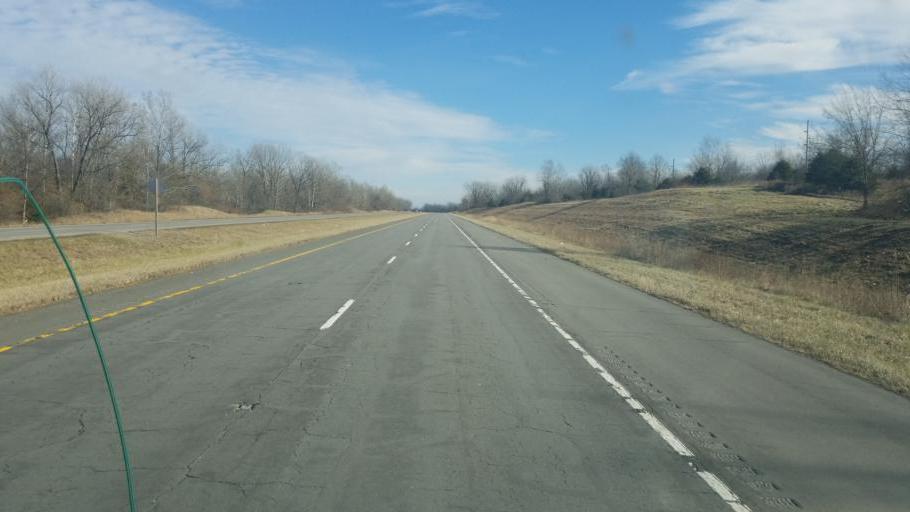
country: US
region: Illinois
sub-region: Saline County
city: Carrier Mills
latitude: 37.7305
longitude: -88.7506
